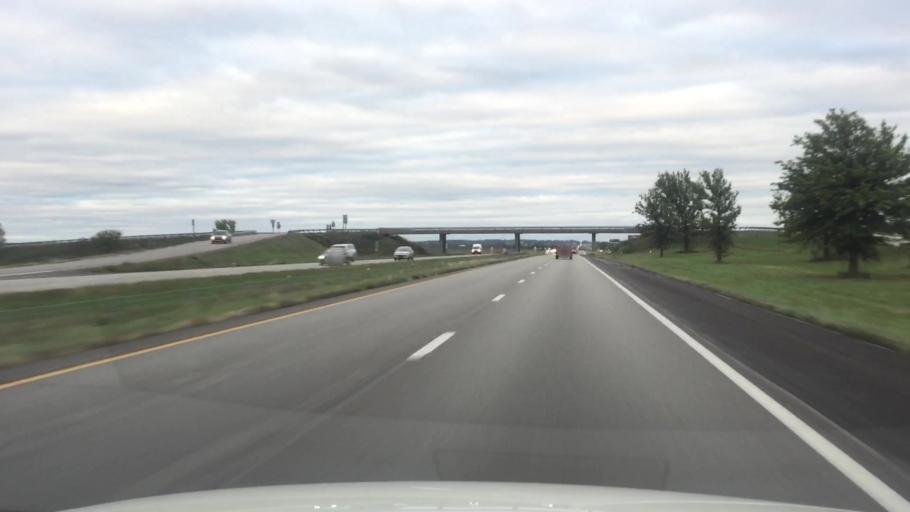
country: US
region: Missouri
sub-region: Jackson County
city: Oak Grove
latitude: 39.0114
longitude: -94.0709
